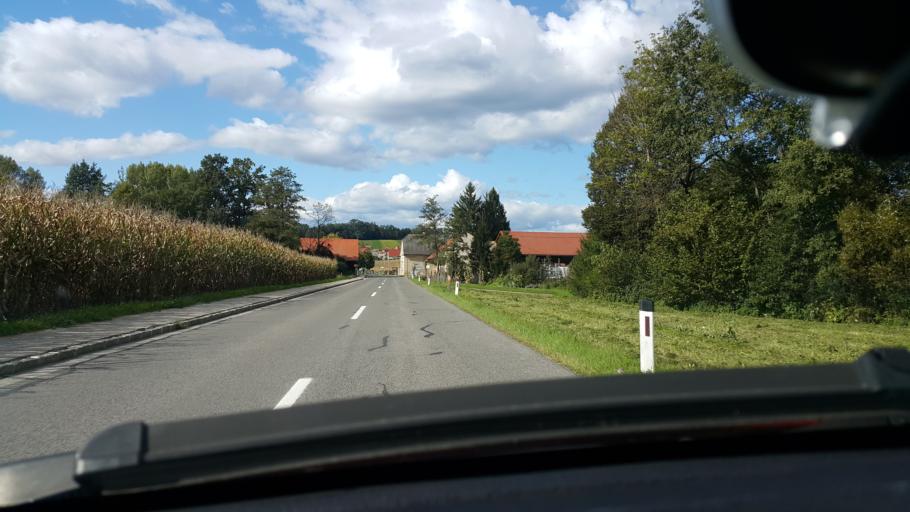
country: AT
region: Styria
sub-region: Politischer Bezirk Deutschlandsberg
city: Wies
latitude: 46.7224
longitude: 15.2950
